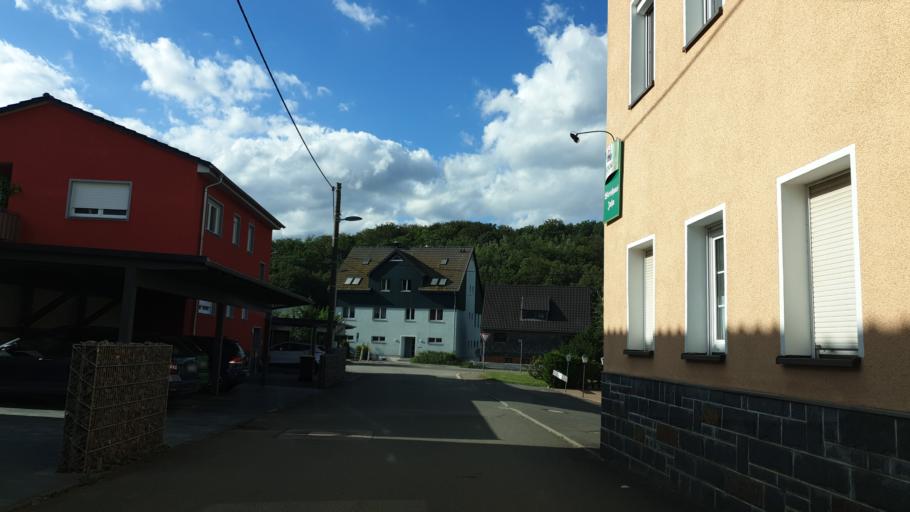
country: DE
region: Saxony
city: Lichtenstein
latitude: 50.7081
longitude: 12.6409
